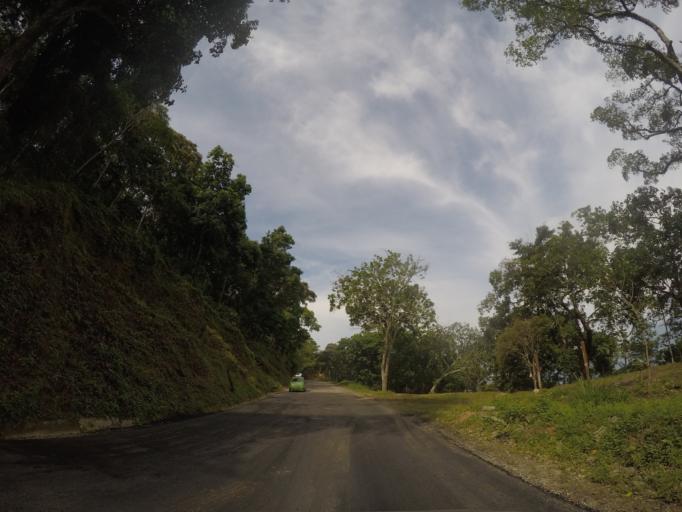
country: MX
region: Oaxaca
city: Pluma Hidalgo
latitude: 15.9438
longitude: -96.4428
